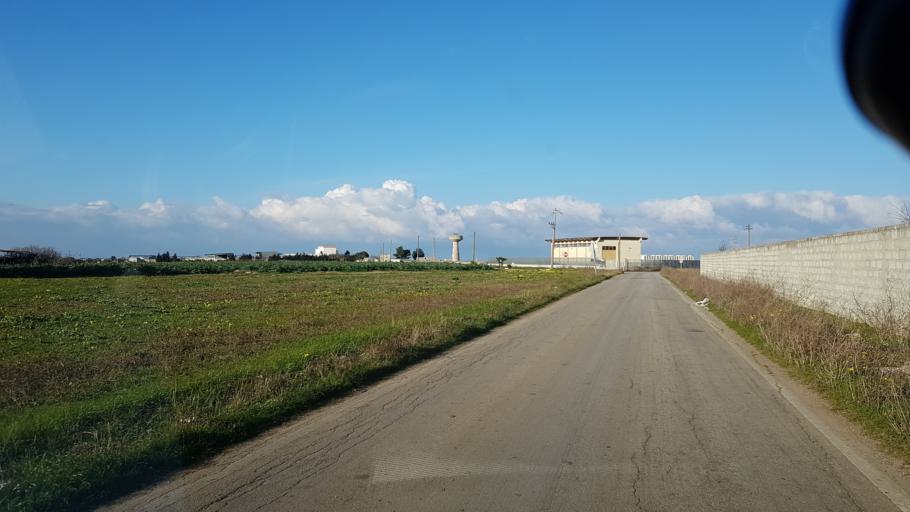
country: IT
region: Apulia
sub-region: Provincia di Brindisi
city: Brindisi
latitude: 40.6025
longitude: 17.9073
